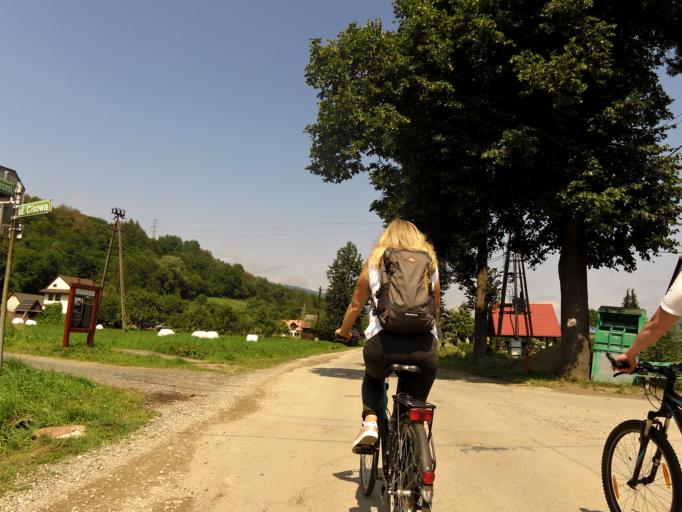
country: PL
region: Silesian Voivodeship
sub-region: Powiat zywiecki
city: Cisiec
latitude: 49.5802
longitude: 19.0912
